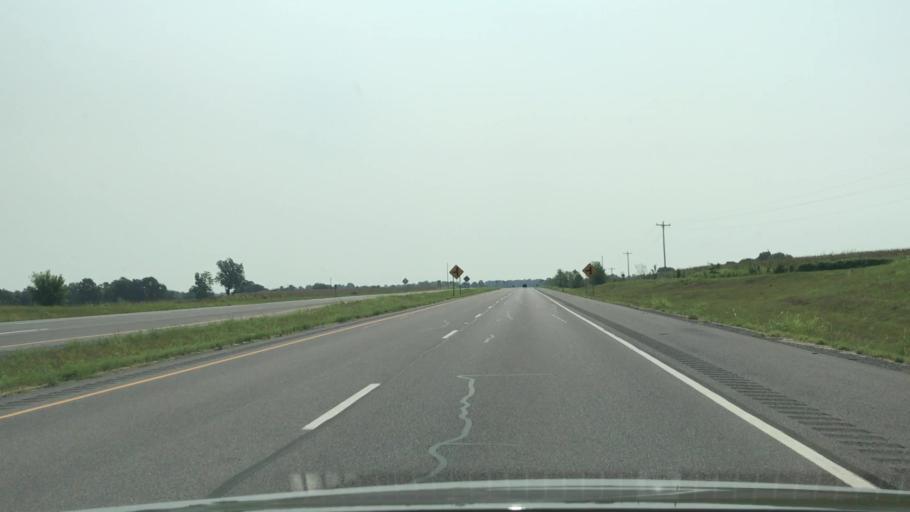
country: US
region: Kentucky
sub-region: Graves County
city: Mayfield
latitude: 36.6857
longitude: -88.5418
